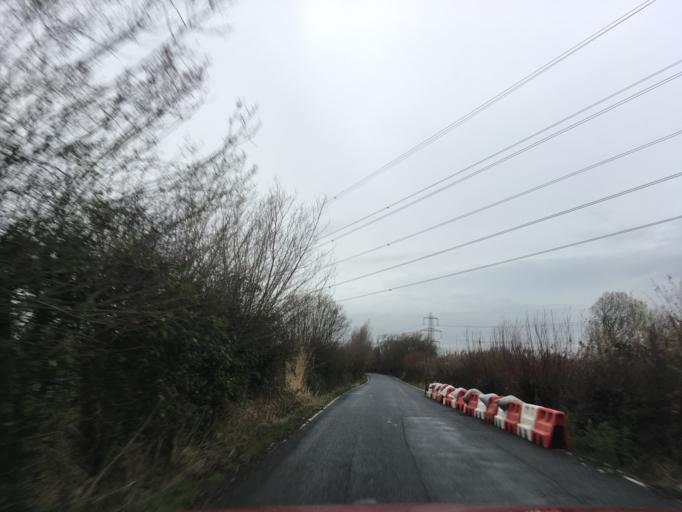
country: GB
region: Wales
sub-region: Newport
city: Bishton
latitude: 51.5597
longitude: -2.8929
